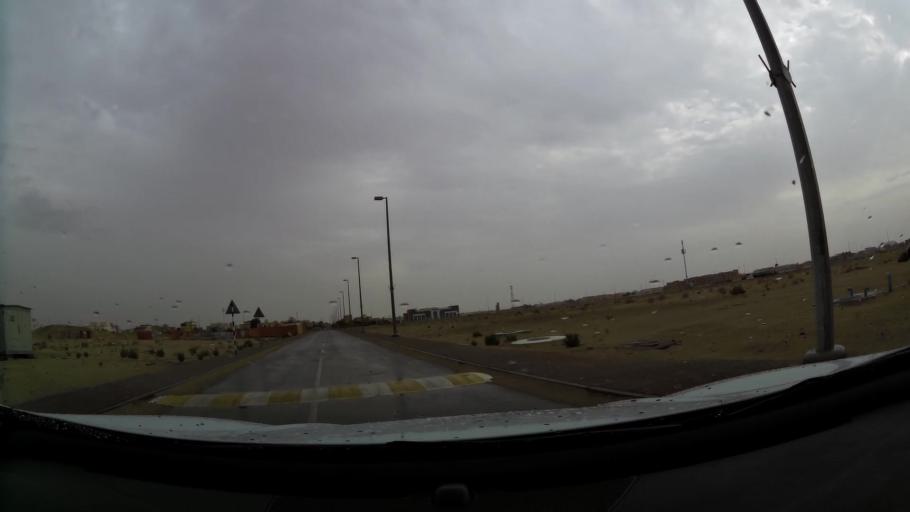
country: AE
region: Abu Dhabi
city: Abu Dhabi
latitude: 24.3685
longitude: 54.6328
